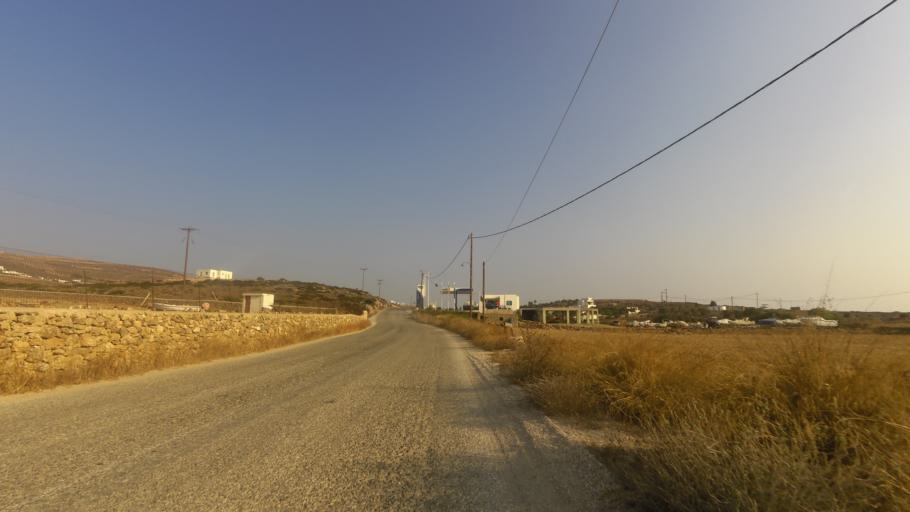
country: GR
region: South Aegean
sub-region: Nomos Kykladon
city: Antiparos
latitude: 37.0277
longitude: 25.0762
